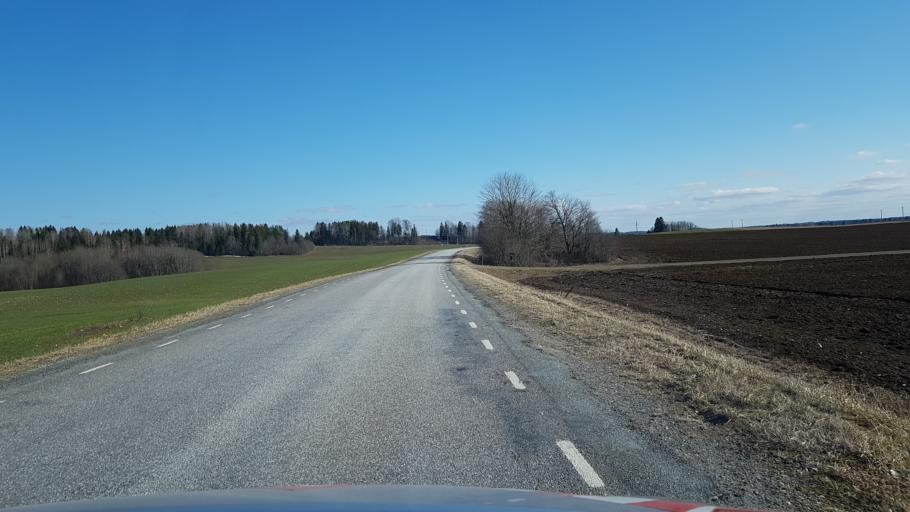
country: EE
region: Laeaene-Virumaa
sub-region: Kadrina vald
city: Kadrina
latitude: 59.3566
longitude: 26.0665
